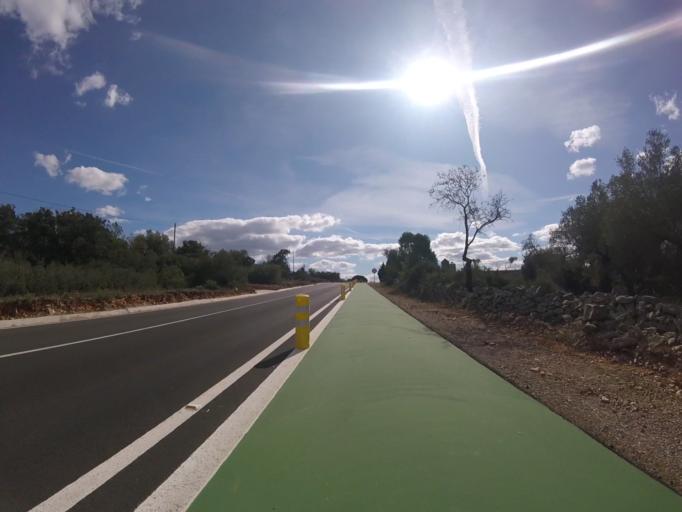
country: ES
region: Valencia
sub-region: Provincia de Castello
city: Albocasser
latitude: 40.4109
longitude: 0.0712
